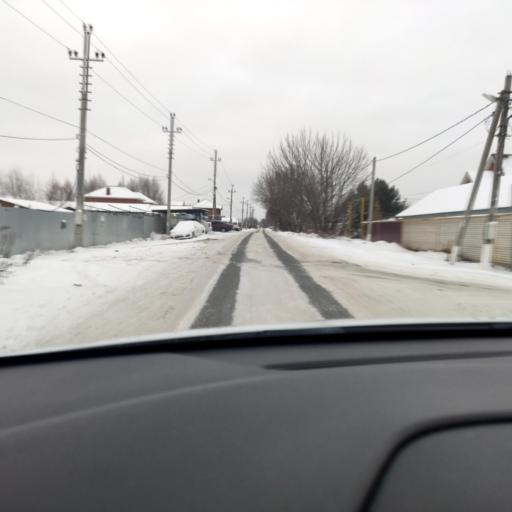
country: RU
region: Tatarstan
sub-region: Gorod Kazan'
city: Kazan
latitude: 55.8703
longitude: 49.1499
